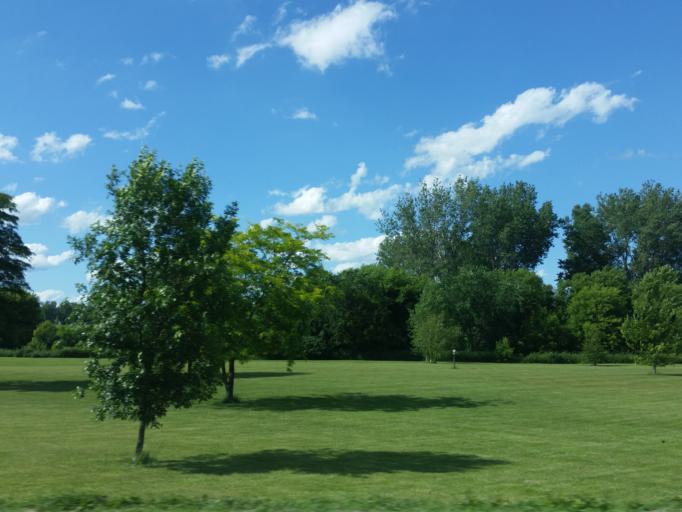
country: US
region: Minnesota
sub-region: Wright County
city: Cokato
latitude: 45.0656
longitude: -94.1964
